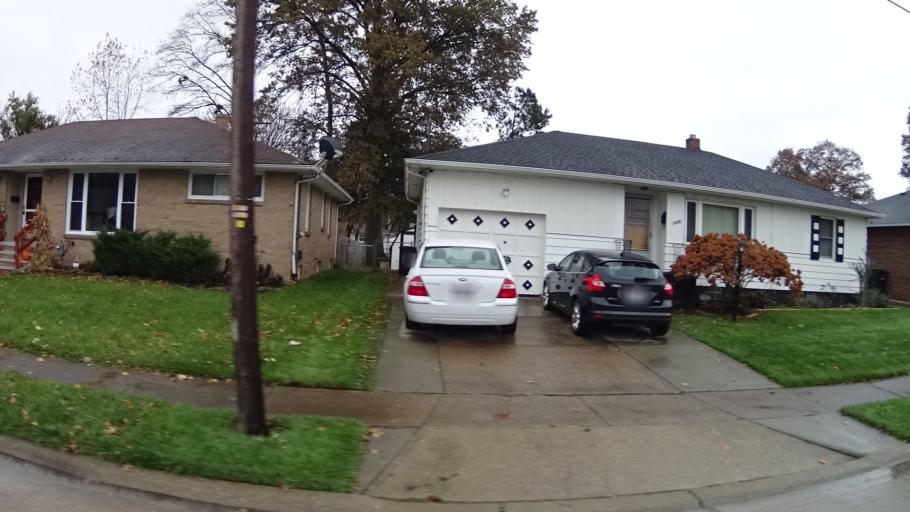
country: US
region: Ohio
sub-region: Lorain County
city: Elyria
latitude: 41.3847
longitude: -82.1352
